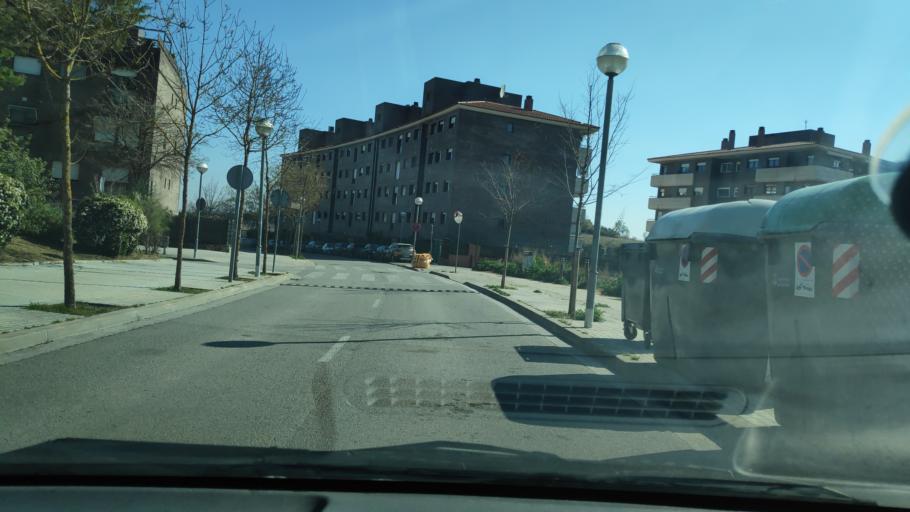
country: ES
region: Catalonia
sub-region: Provincia de Barcelona
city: Sant Quirze del Valles
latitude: 41.5545
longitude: 2.0740
